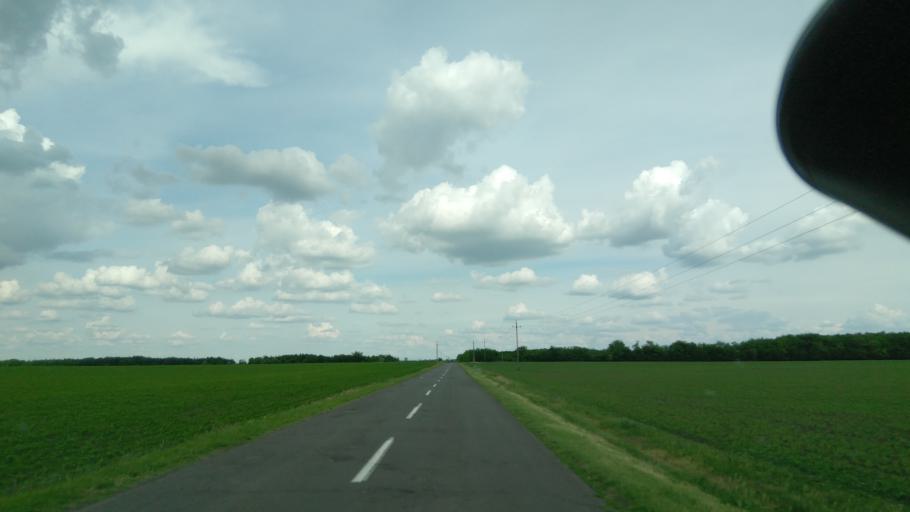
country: RO
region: Arad
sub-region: Comuna Peregu Mare
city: Peregu Mic
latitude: 46.3021
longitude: 20.9214
